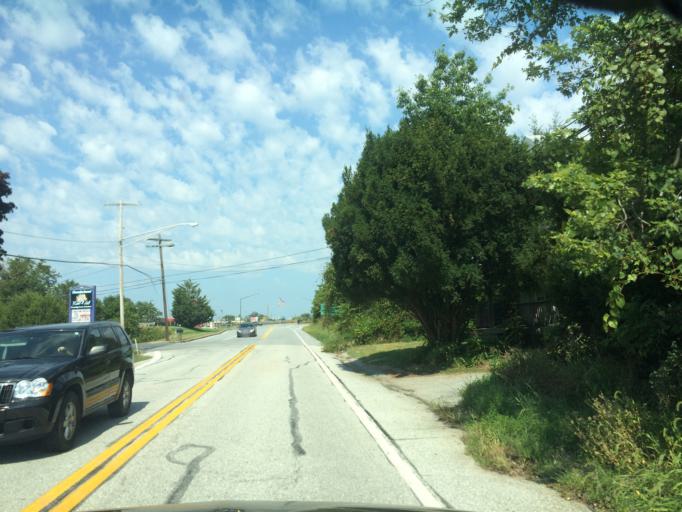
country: US
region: Maryland
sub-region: Carroll County
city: Taneytown
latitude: 39.6469
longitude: -77.1521
